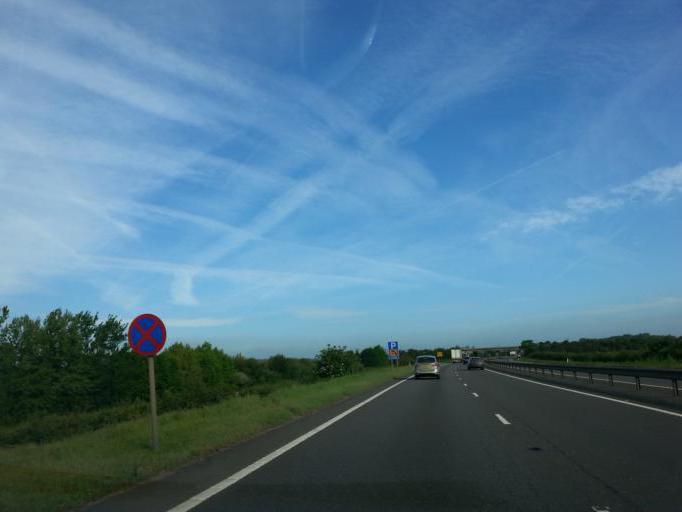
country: GB
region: England
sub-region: Nottinghamshire
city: Newark on Trent
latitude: 53.1072
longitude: -0.8096
